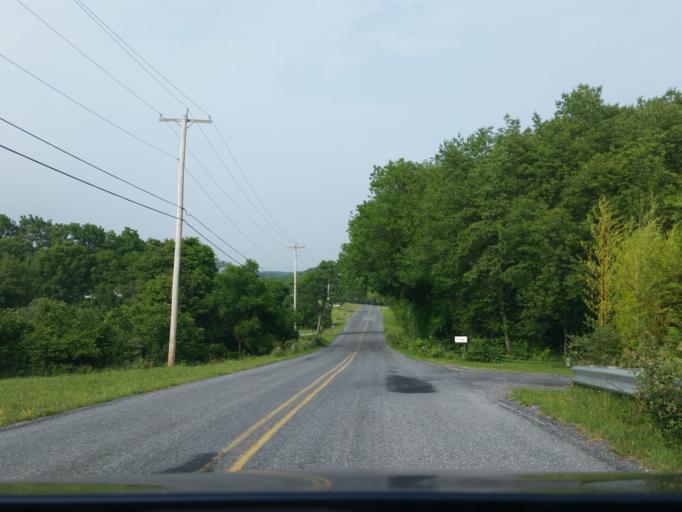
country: US
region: Pennsylvania
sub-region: Lebanon County
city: Palmyra
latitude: 40.4086
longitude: -76.6013
